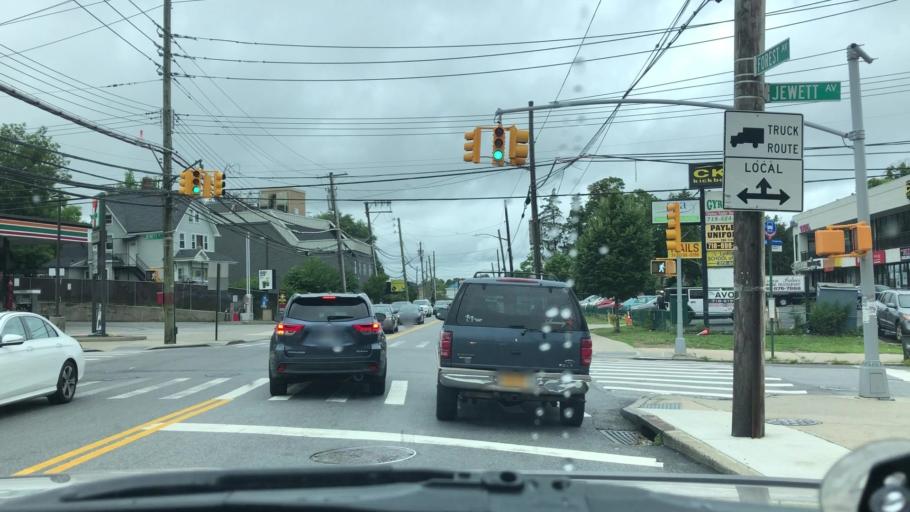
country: US
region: New Jersey
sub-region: Hudson County
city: Bayonne
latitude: 40.6264
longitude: -74.1311
